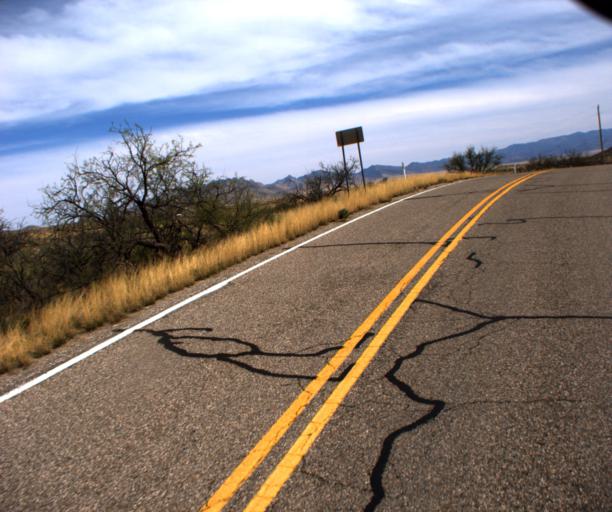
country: US
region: Arizona
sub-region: Cochise County
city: Willcox
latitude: 32.1590
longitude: -109.5665
